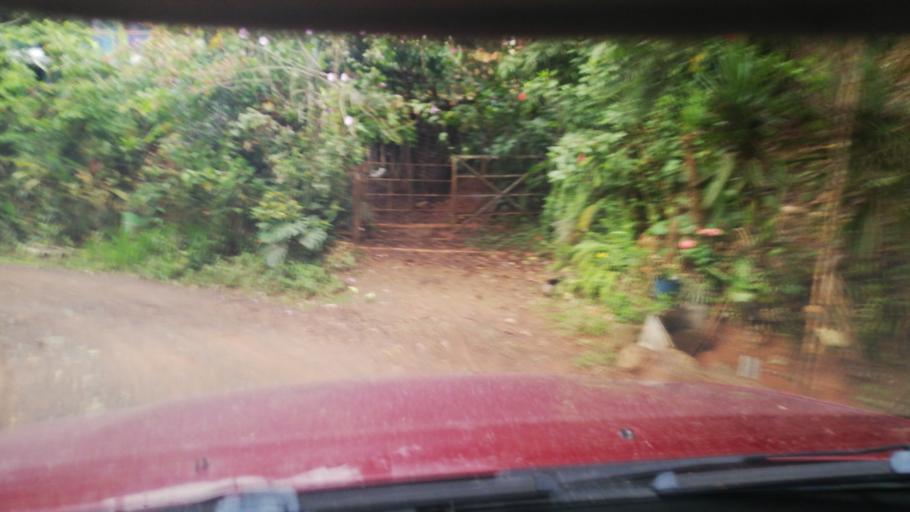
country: CO
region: Risaralda
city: La Virginia
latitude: 4.8815
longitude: -75.9489
